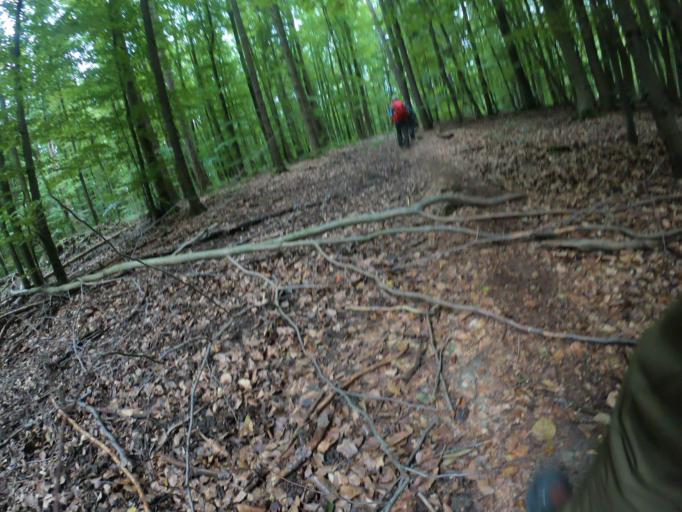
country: DE
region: Hesse
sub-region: Regierungsbezirk Darmstadt
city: Wiesbaden
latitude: 50.1146
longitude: 8.2532
